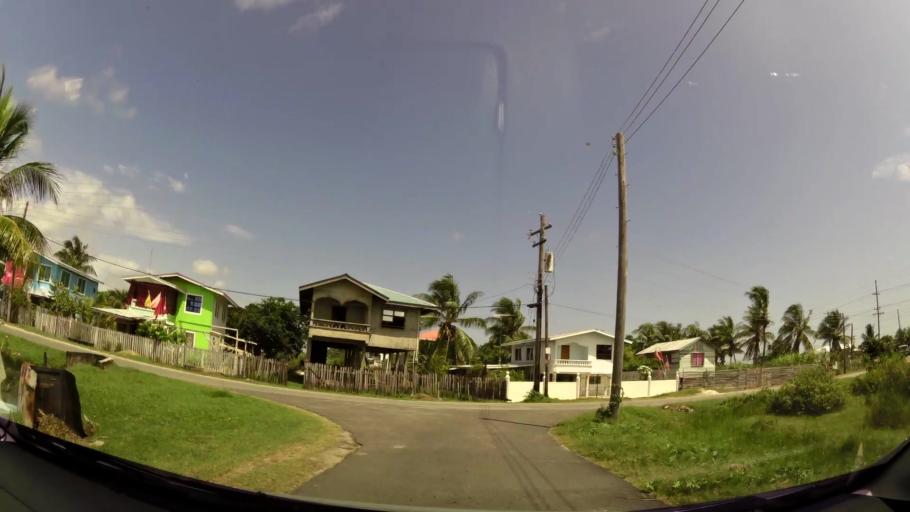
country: GY
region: Demerara-Mahaica
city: Mahaica Village
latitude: 6.7757
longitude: -58.0127
